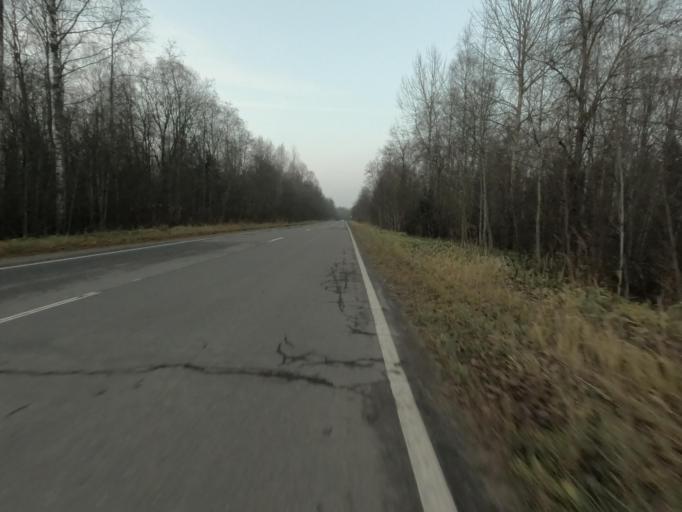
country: RU
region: Leningrad
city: Kirovsk
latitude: 59.8542
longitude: 30.9920
